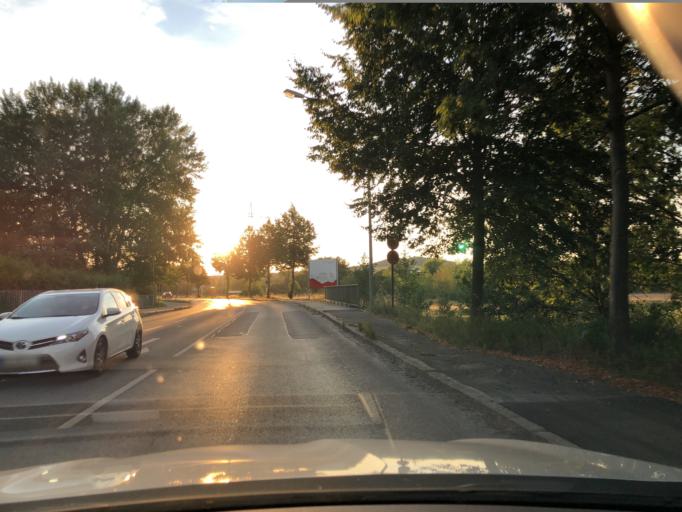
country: DE
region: Bavaria
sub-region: Upper Palatinate
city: Poppenricht
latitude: 49.4909
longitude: 11.7843
